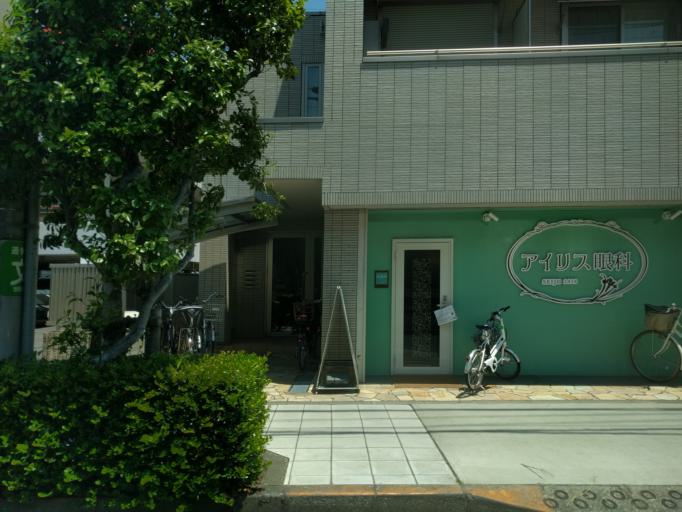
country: JP
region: Tokyo
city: Chofugaoka
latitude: 35.6407
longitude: 139.5970
